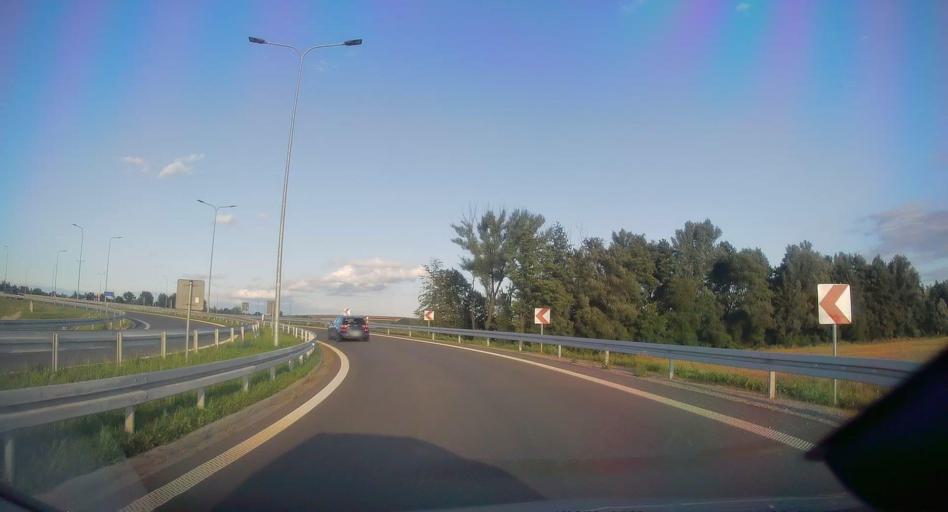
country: PL
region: Lesser Poland Voivodeship
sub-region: Powiat wielicki
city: Podleze
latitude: 50.0092
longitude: 20.1577
